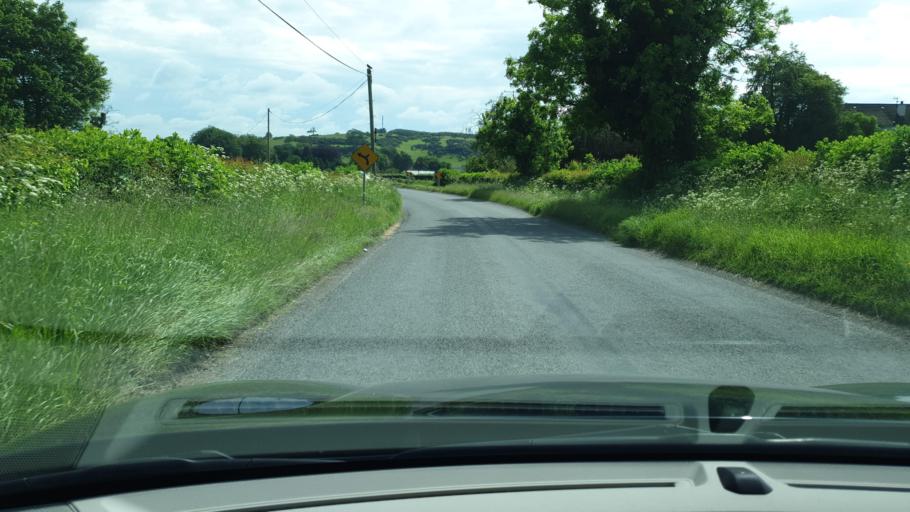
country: IE
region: Leinster
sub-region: An Mhi
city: Slane
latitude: 53.7177
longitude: -6.5754
